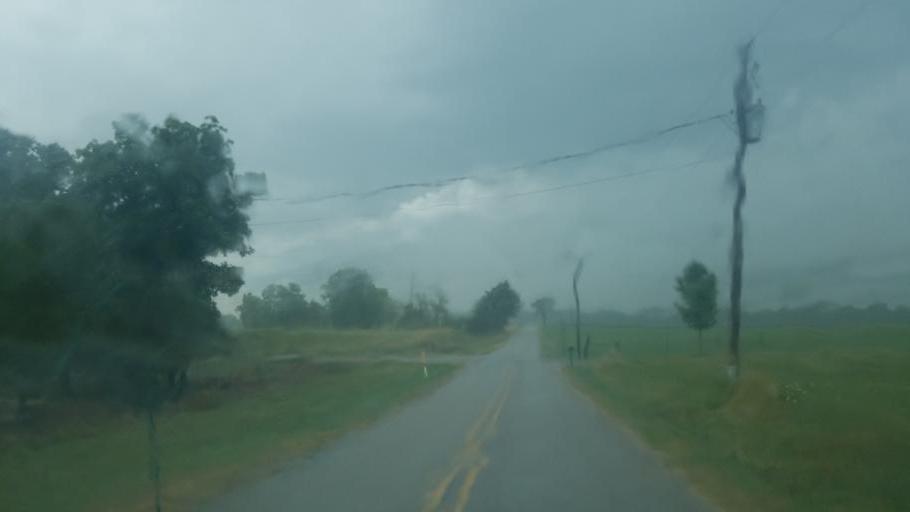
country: US
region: Indiana
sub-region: DeKalb County
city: Butler
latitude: 41.4656
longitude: -84.8334
